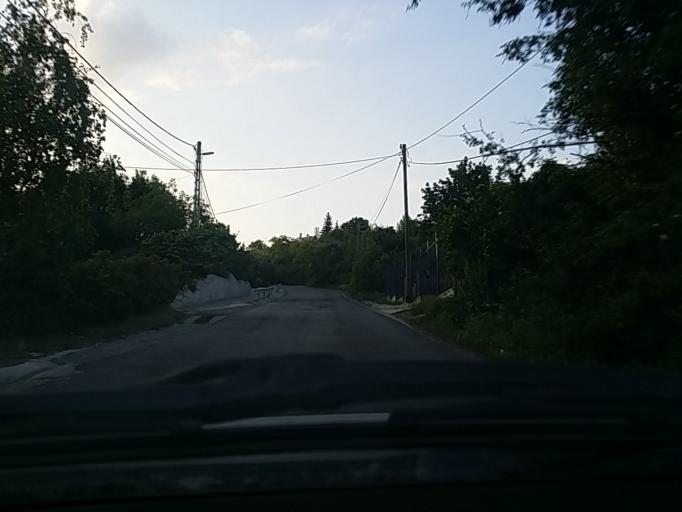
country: HU
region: Pest
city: Urom
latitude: 47.5901
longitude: 19.0335
